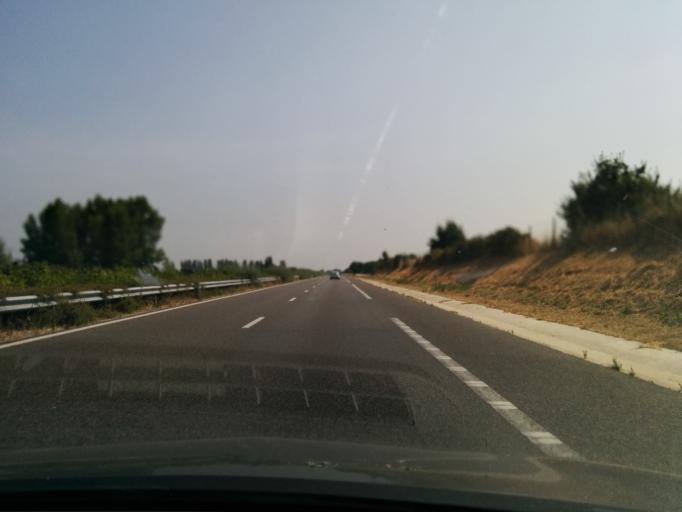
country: FR
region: Midi-Pyrenees
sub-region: Departement du Tarn
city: Giroussens
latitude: 43.7978
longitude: 1.7657
